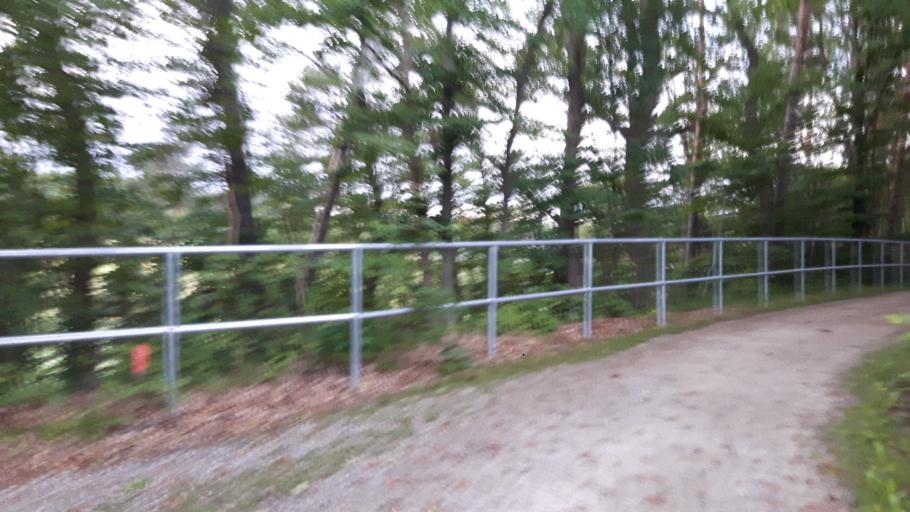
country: DE
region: Thuringia
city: Buchfart
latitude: 50.9214
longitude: 11.3373
